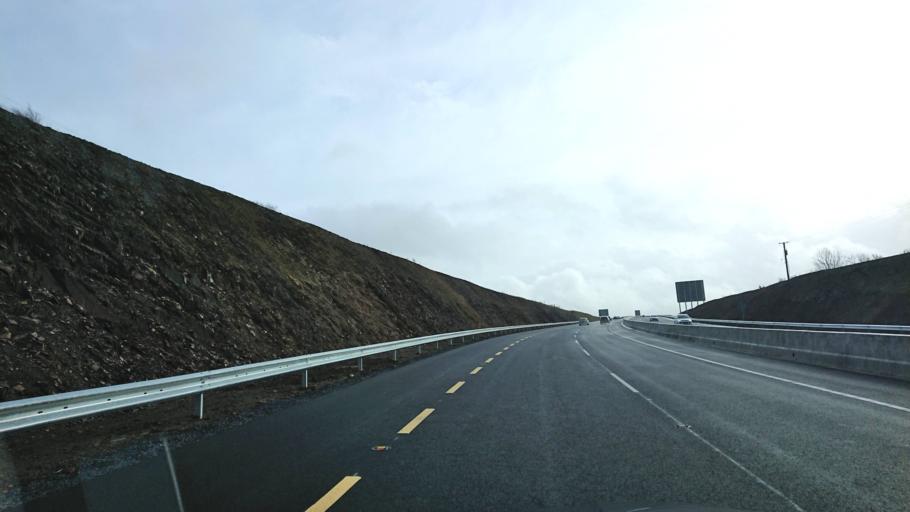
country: IE
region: Leinster
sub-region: Loch Garman
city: New Ross
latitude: 52.3602
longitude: -7.0085
